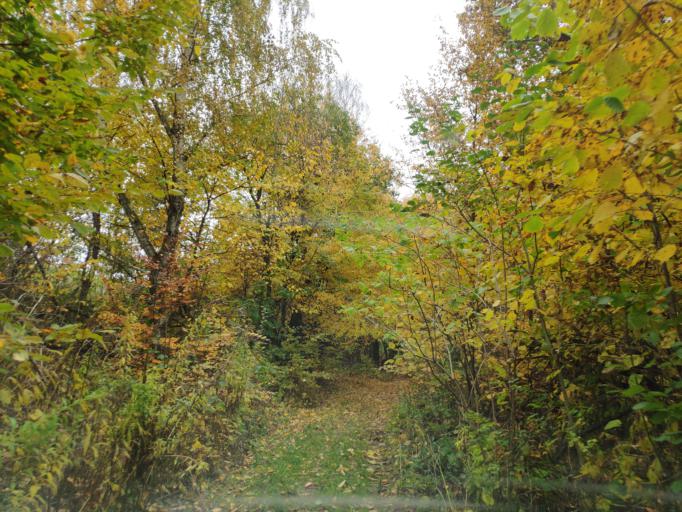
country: SK
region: Kosicky
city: Moldava nad Bodvou
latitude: 48.7244
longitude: 21.0988
